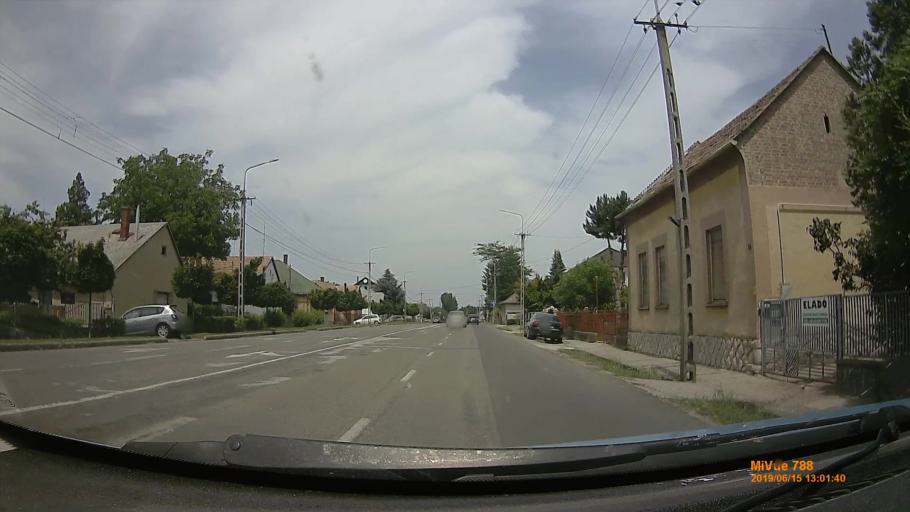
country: HU
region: Tolna
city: Dombovar
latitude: 46.3810
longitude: 18.1310
